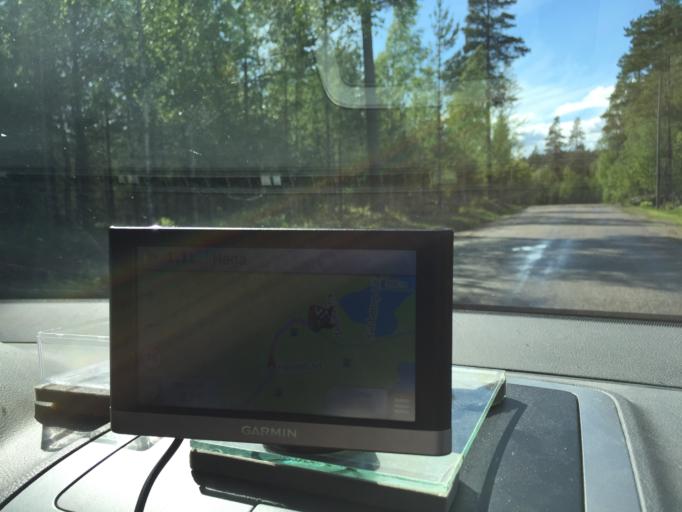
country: SE
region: Soedermanland
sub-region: Vingakers Kommun
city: Vingaker
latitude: 58.9866
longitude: 15.6742
